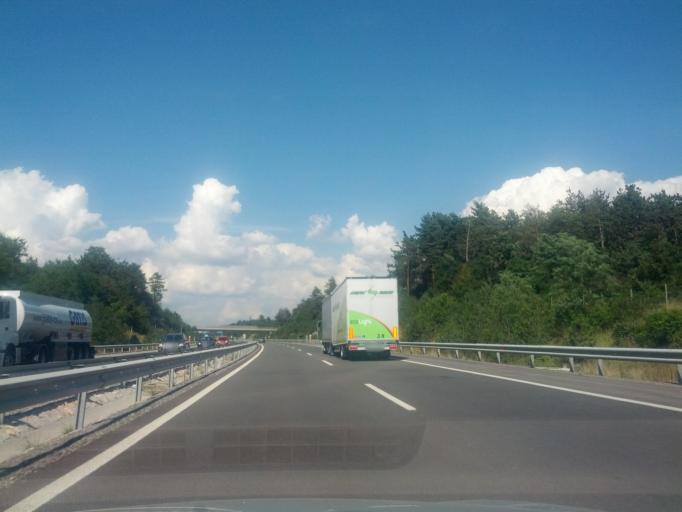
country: SI
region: Hrpelje-Kozina
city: Kozina
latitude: 45.6202
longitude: 13.9531
